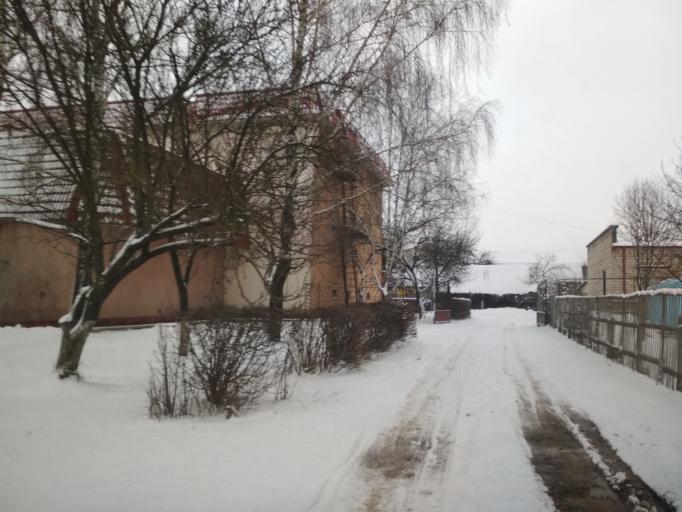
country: BY
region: Minsk
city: Mar''ina Horka
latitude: 53.5092
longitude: 28.1448
